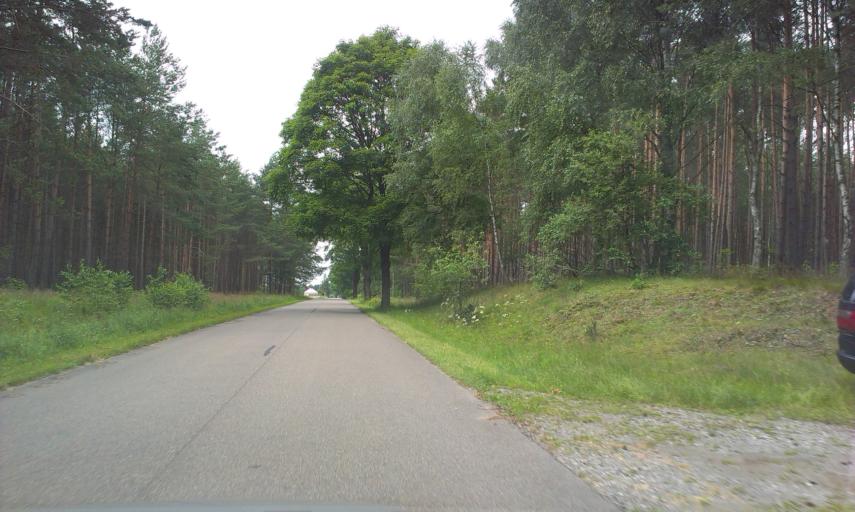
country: PL
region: West Pomeranian Voivodeship
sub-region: Powiat szczecinecki
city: Lubowo
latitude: 53.6444
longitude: 16.3202
